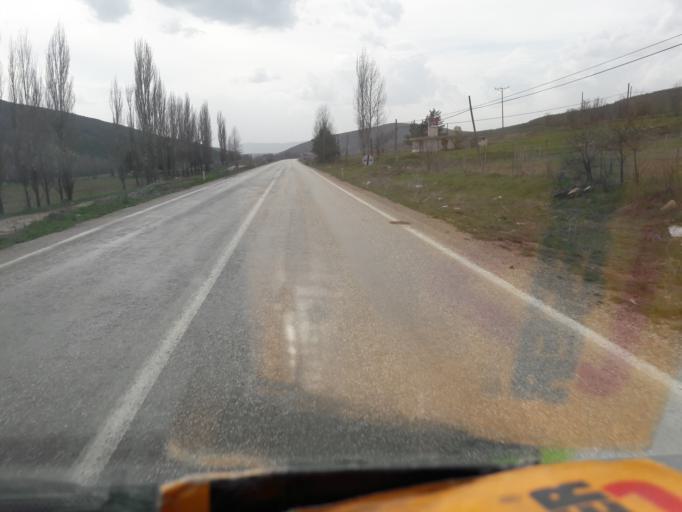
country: TR
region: Gumushane
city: Siran
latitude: 40.1725
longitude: 39.1701
